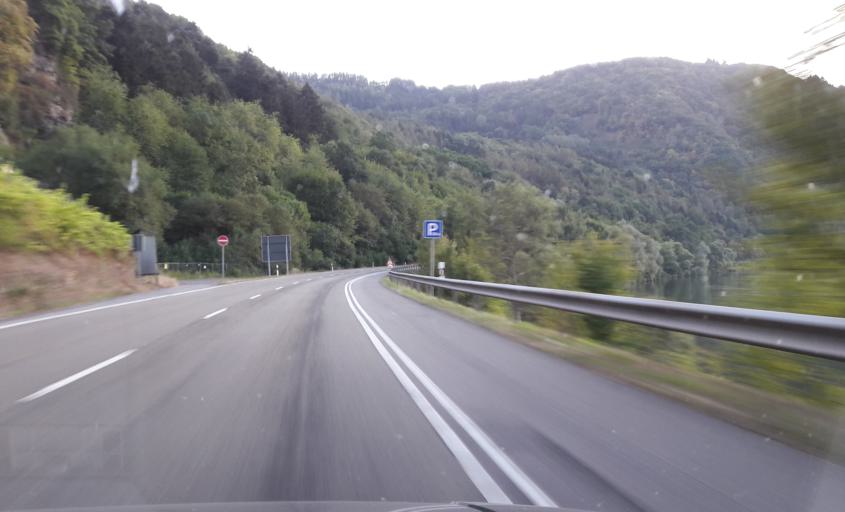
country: DE
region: Rheinland-Pfalz
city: Zell
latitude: 50.0141
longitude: 7.1771
